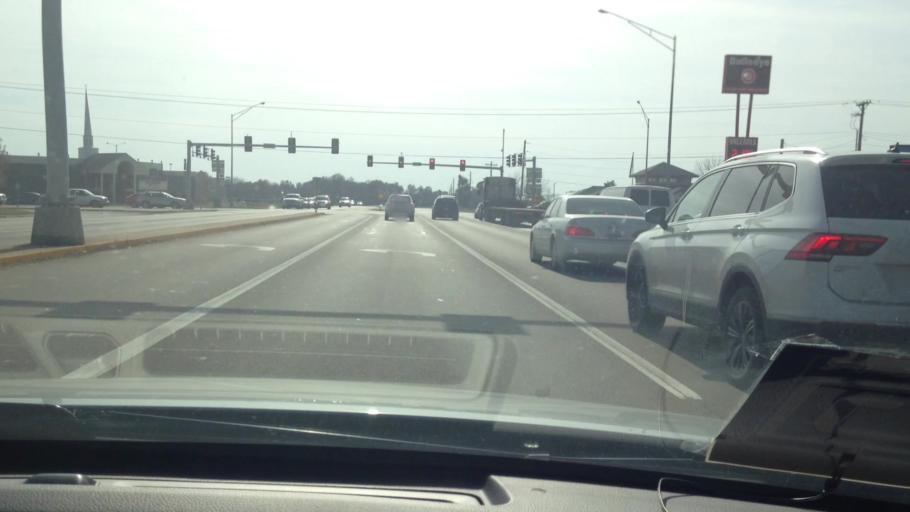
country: US
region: Missouri
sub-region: Henry County
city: Clinton
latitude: 38.3671
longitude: -93.7521
